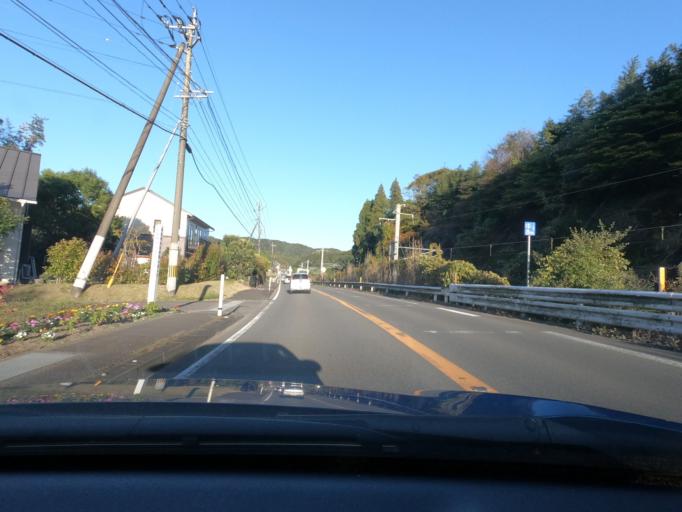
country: JP
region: Kagoshima
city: Satsumasendai
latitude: 31.8474
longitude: 130.2576
